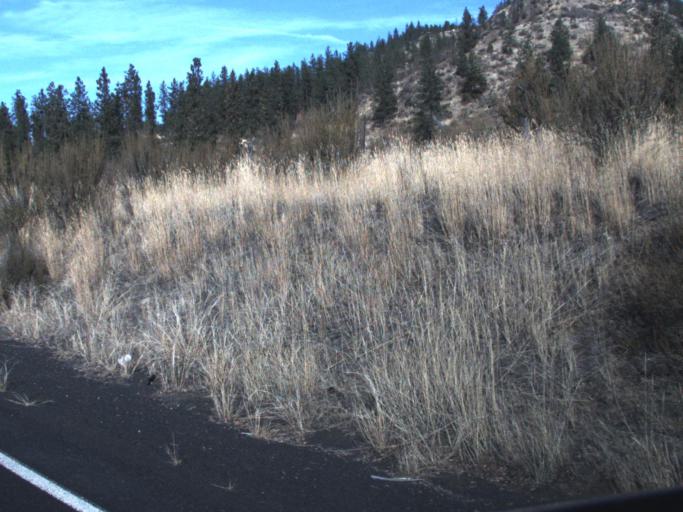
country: US
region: Washington
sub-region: Lincoln County
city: Davenport
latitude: 47.8960
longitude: -118.2738
